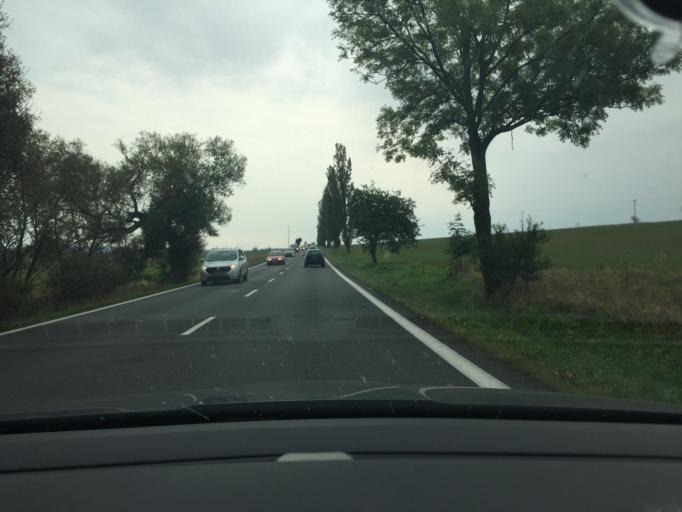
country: CZ
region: Central Bohemia
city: Milin
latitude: 49.6168
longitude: 14.0549
